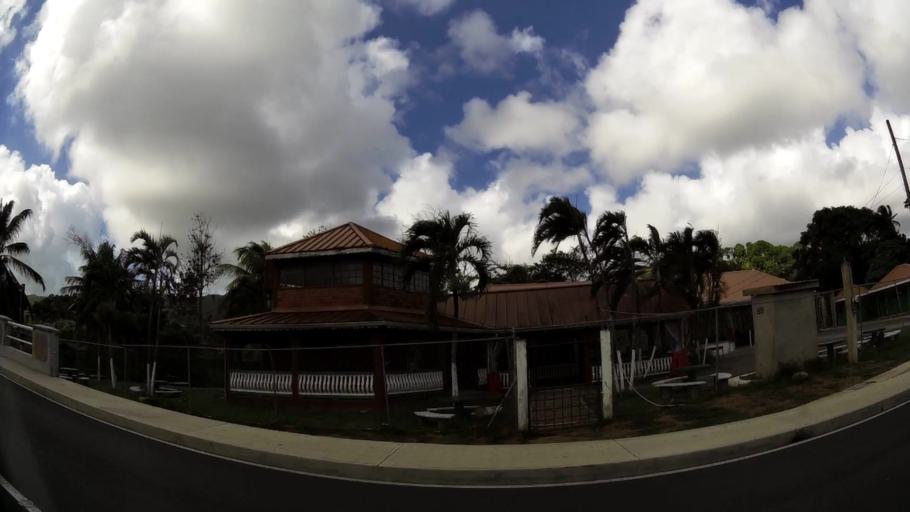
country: LC
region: Dennery Quarter
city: Dennery
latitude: 13.9322
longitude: -60.9305
